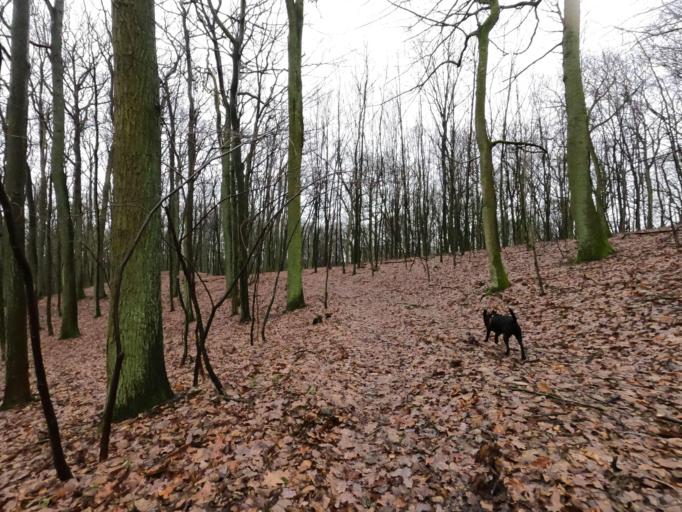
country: PL
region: Greater Poland Voivodeship
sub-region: Powiat pilski
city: Osiek nad Notecia
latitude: 53.1233
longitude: 17.2666
